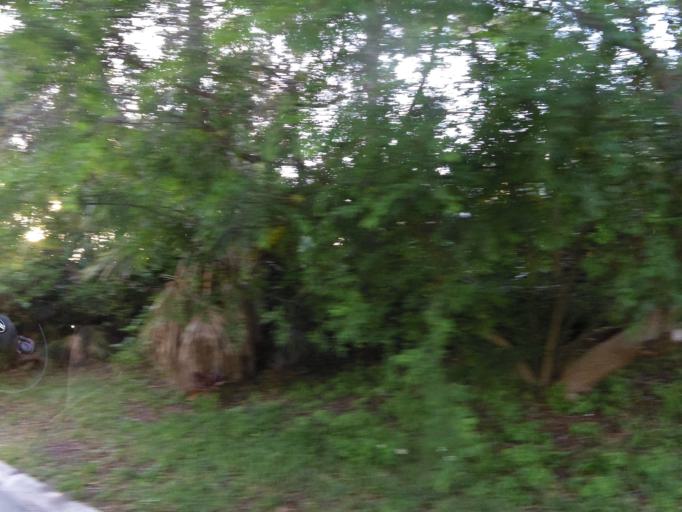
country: US
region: Florida
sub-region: Duval County
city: Neptune Beach
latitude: 30.3211
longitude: -81.4164
